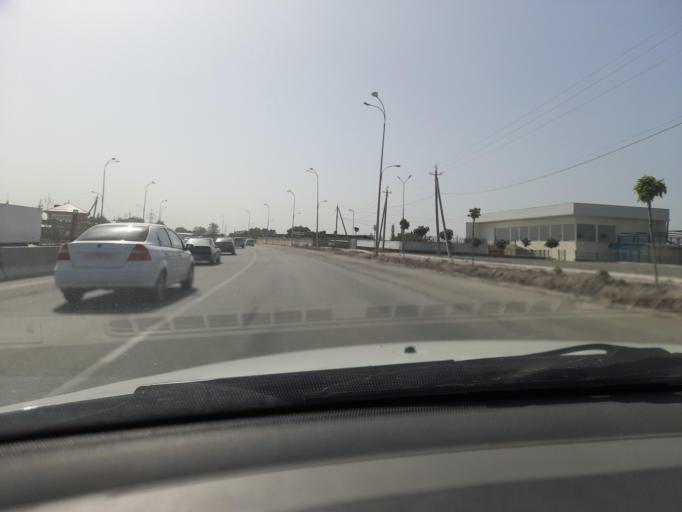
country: UZ
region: Samarqand
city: Samarqand
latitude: 39.7117
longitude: 66.9750
